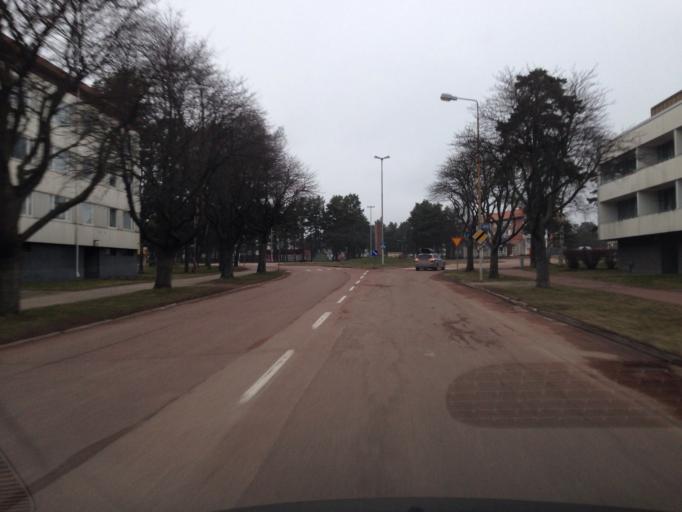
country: AX
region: Mariehamns stad
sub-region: Mariehamn
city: Mariehamn
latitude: 60.1037
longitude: 19.9373
